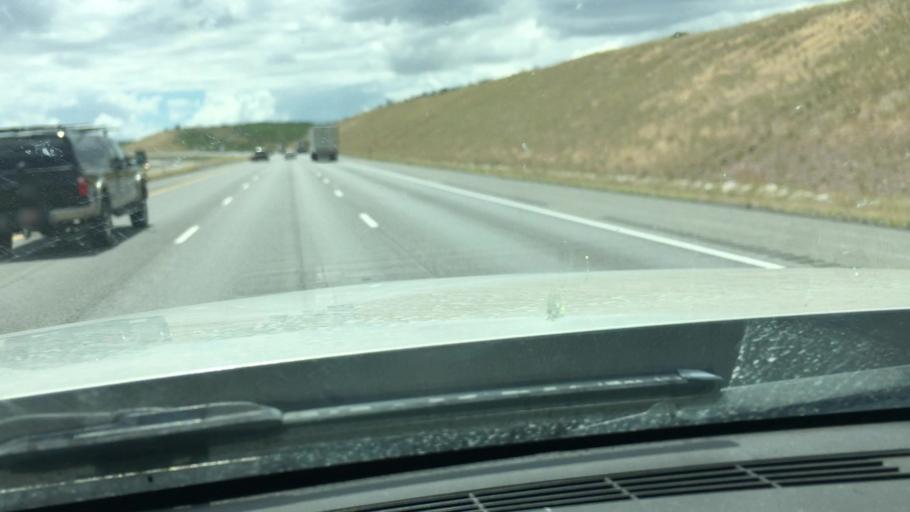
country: US
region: Utah
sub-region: Beaver County
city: Beaver
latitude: 38.4917
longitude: -112.6177
